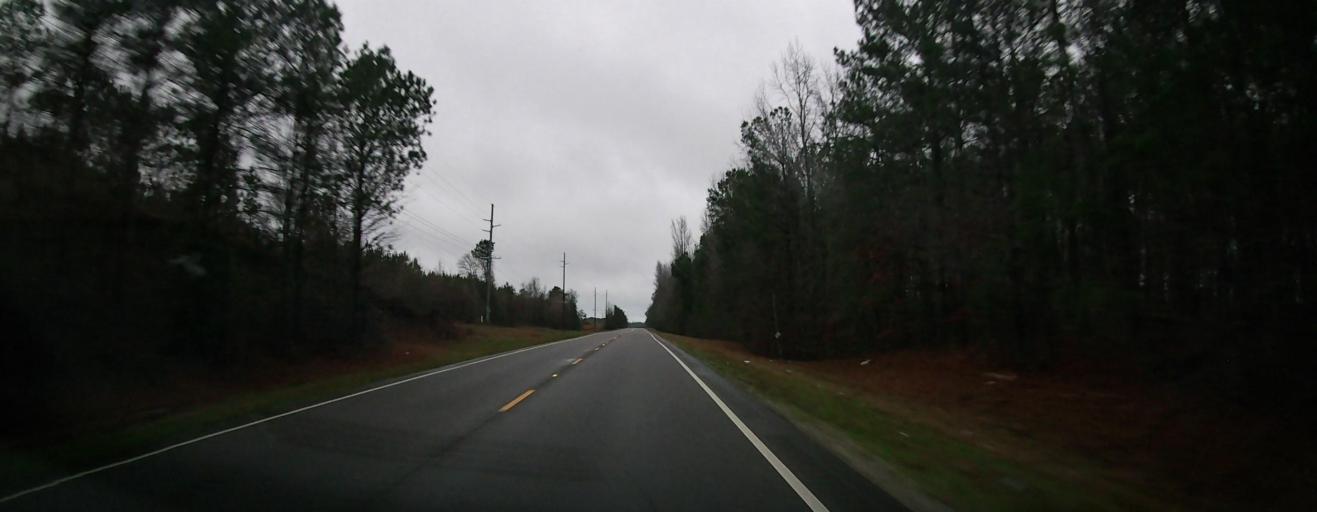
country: US
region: Alabama
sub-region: Bibb County
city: West Blocton
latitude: 33.0986
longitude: -87.1381
